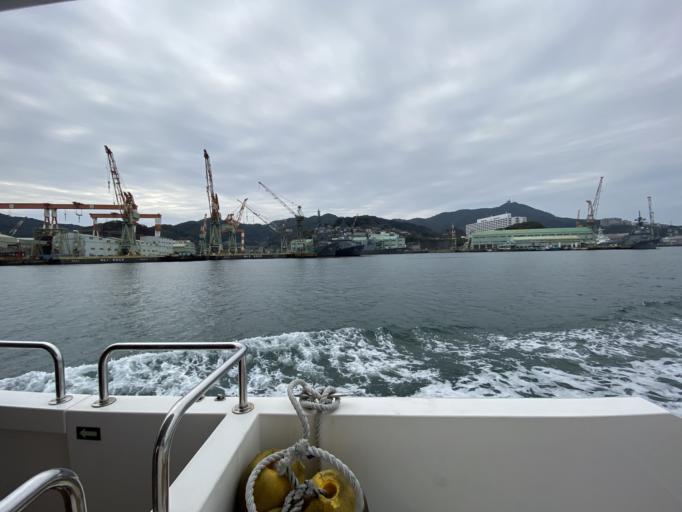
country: JP
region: Nagasaki
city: Nagasaki-shi
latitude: 32.7335
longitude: 129.8597
